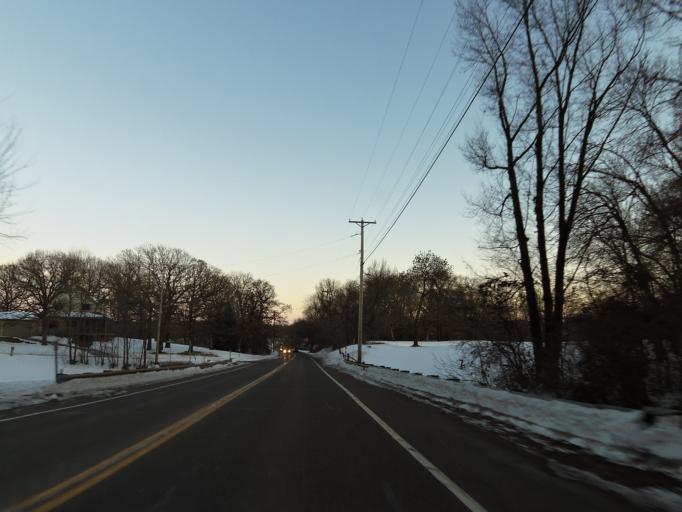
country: US
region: Minnesota
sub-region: Washington County
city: Dellwood
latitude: 45.0927
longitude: -92.9666
